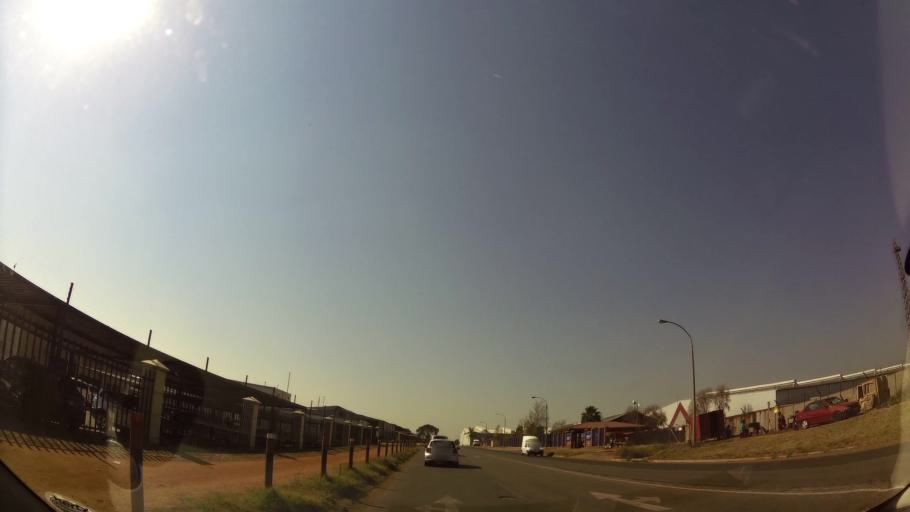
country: ZA
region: Gauteng
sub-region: Ekurhuleni Metropolitan Municipality
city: Boksburg
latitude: -26.1712
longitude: 28.2212
